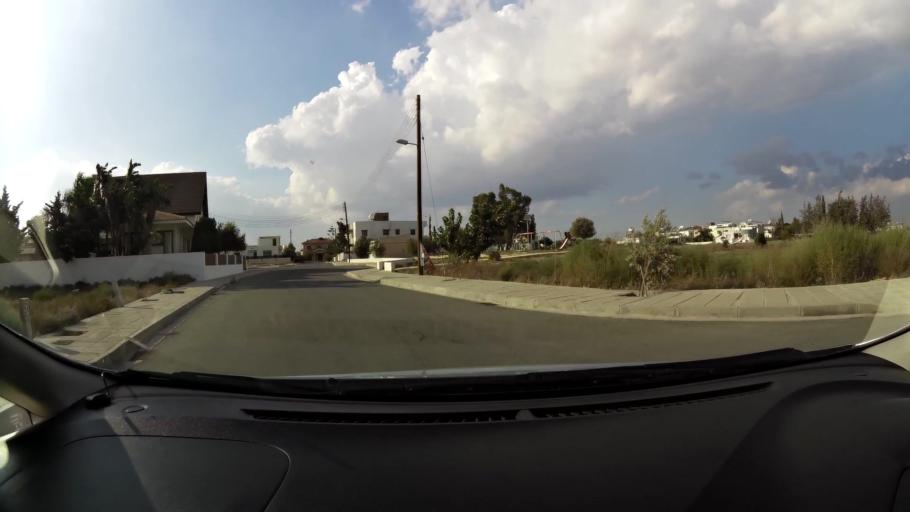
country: CY
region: Larnaka
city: Dhromolaxia
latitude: 34.8797
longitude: 33.5856
